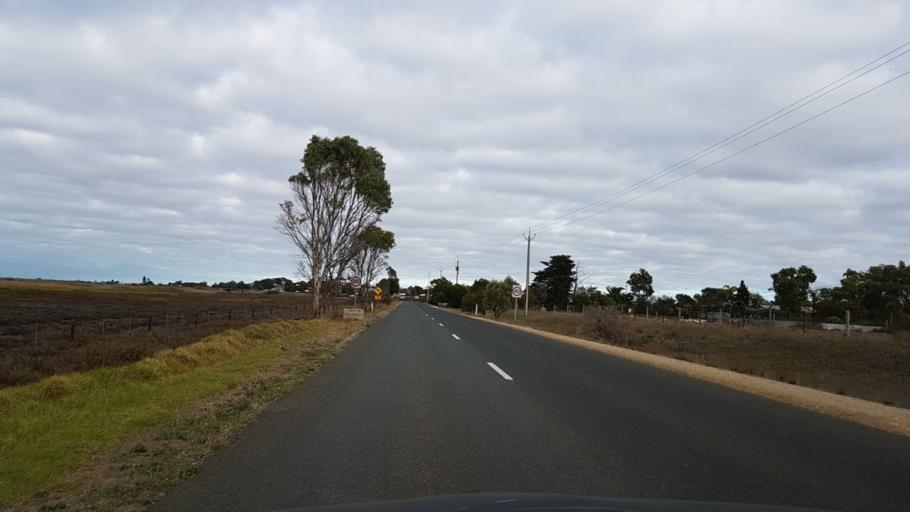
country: AU
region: South Australia
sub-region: Alexandrina
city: Langhorne Creek
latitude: -35.3991
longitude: 138.9872
